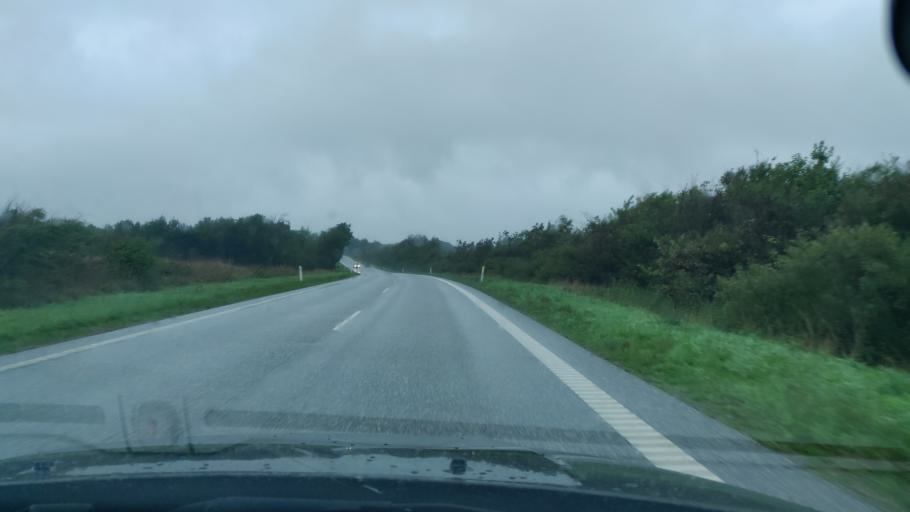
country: DK
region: North Denmark
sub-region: Thisted Kommune
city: Hurup
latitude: 56.8270
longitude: 8.5014
